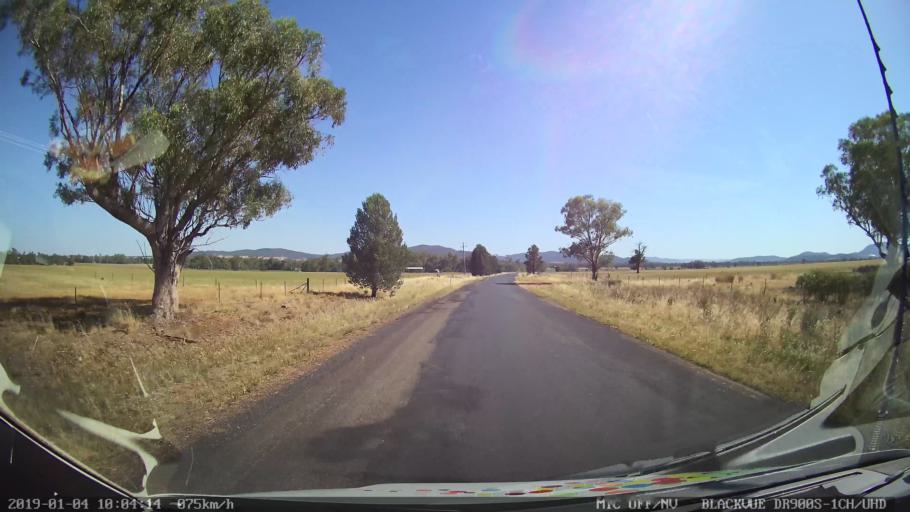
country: AU
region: New South Wales
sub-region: Cabonne
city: Canowindra
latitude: -33.4550
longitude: 148.3609
